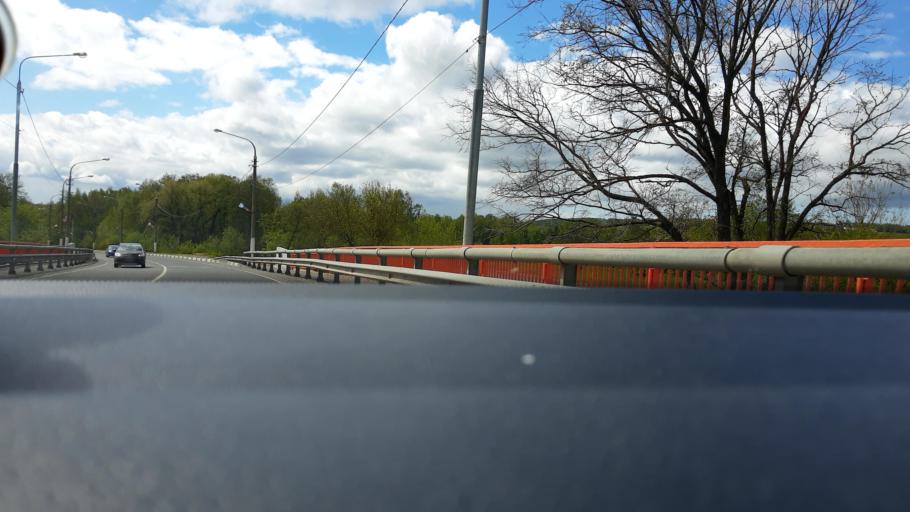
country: RU
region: Moskovskaya
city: Dmitrov
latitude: 56.3261
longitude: 37.4987
